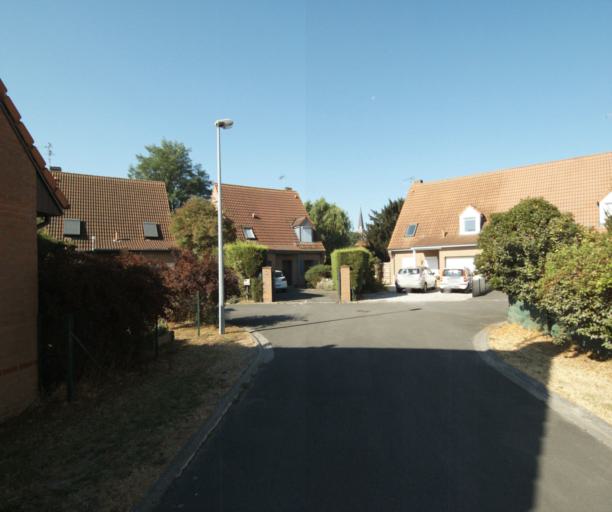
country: FR
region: Nord-Pas-de-Calais
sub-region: Departement du Nord
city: Wervicq-Sud
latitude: 50.7739
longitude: 3.0467
